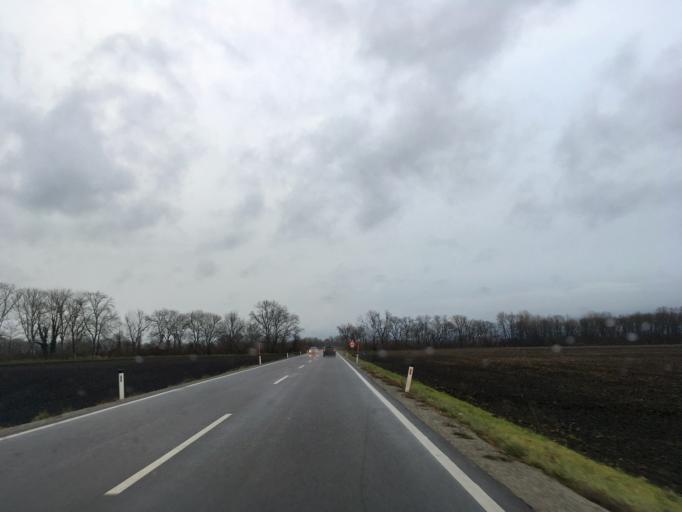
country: AT
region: Lower Austria
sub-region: Politischer Bezirk Wien-Umgebung
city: Ebergassing
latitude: 48.0421
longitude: 16.5276
